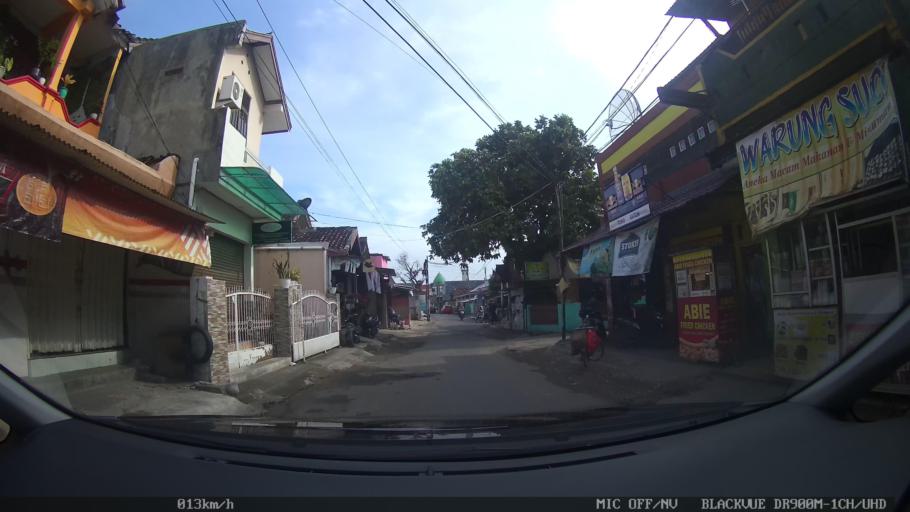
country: ID
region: Lampung
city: Bandarlampung
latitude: -5.4125
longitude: 105.2655
